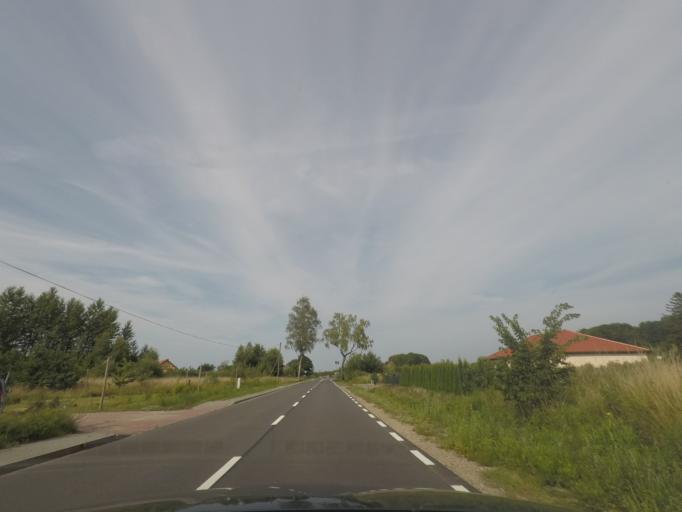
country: PL
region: Pomeranian Voivodeship
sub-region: Powiat slupski
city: Smoldzino
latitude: 54.5989
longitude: 17.1013
